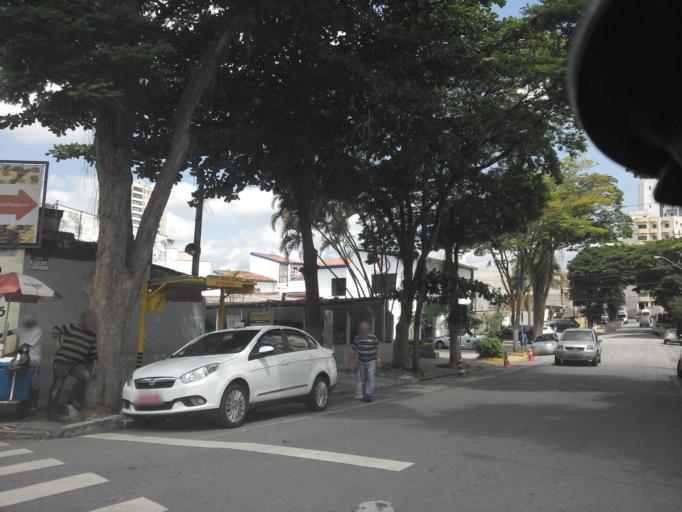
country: BR
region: Sao Paulo
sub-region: Taubate
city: Taubate
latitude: -23.0217
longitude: -45.5564
